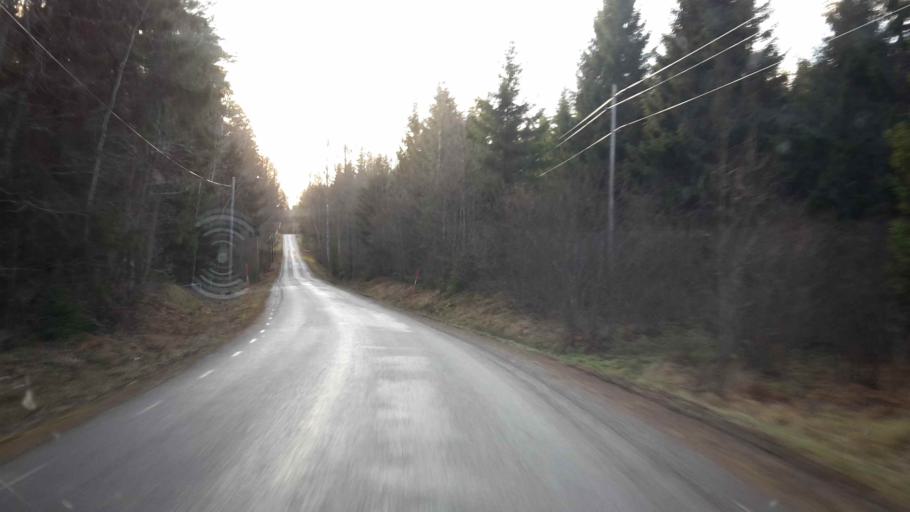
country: SE
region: OEstergoetland
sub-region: Atvidabergs Kommun
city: Atvidaberg
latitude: 58.2679
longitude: 16.1429
